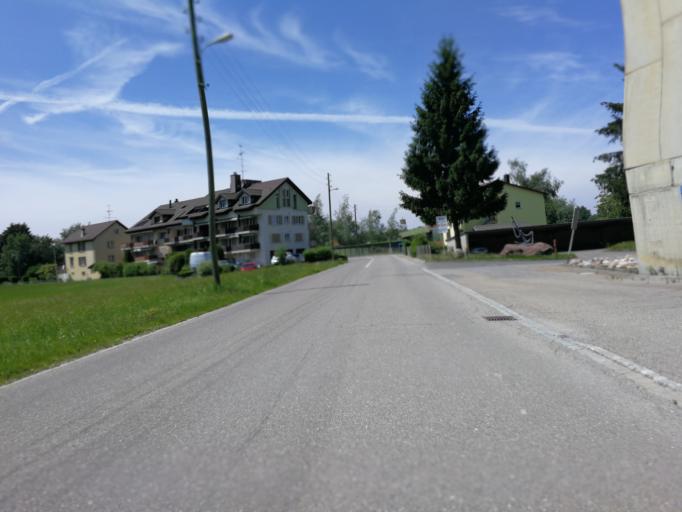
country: CH
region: Schwyz
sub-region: Bezirk March
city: Lachen
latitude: 47.2050
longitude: 8.8922
